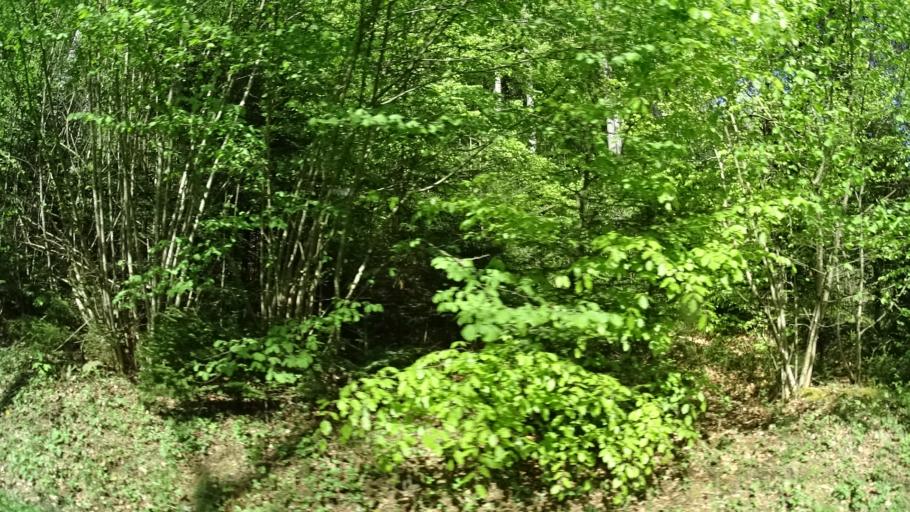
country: DE
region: Baden-Wuerttemberg
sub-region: Karlsruhe Region
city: Hofen an der Enz
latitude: 48.7962
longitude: 8.5523
